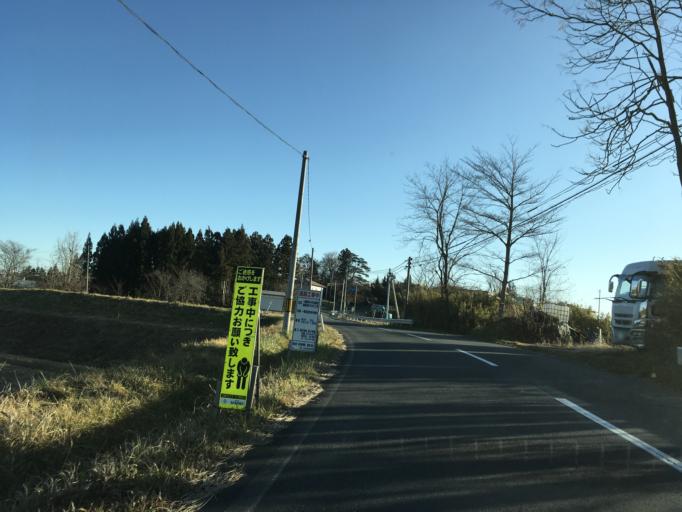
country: JP
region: Iwate
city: Ichinoseki
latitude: 38.7835
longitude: 141.2228
